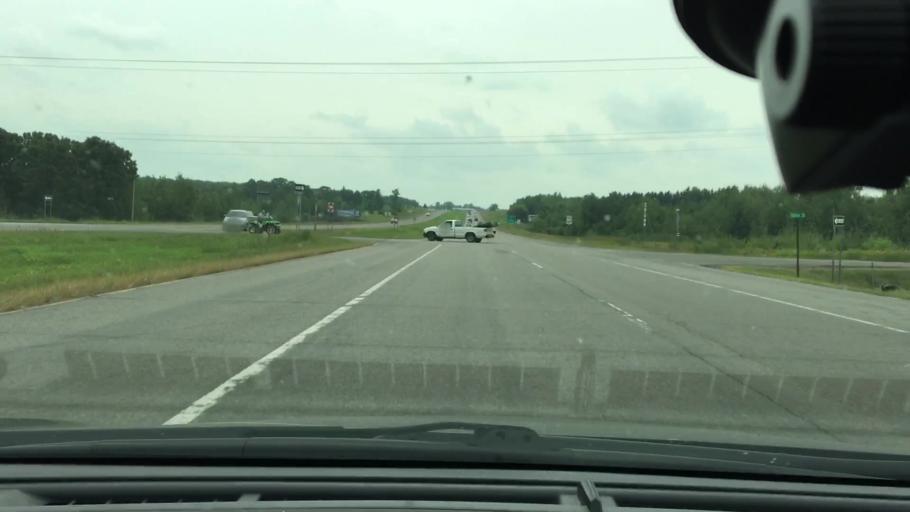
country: US
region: Minnesota
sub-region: Mille Lacs County
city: Milaca
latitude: 45.7793
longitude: -93.6488
